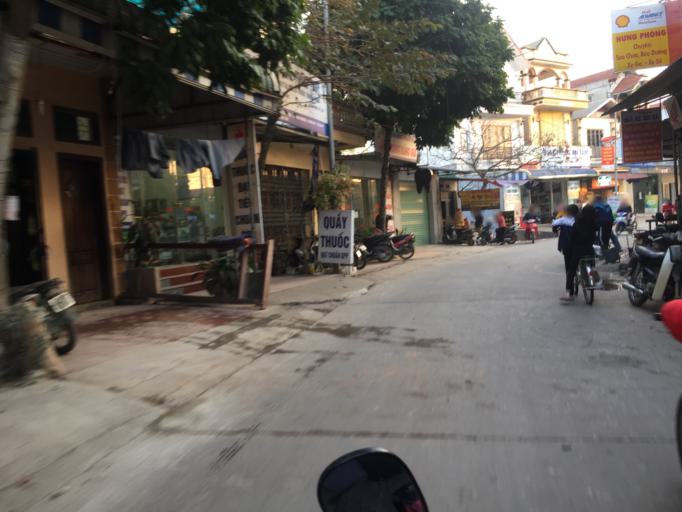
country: VN
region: Ha Noi
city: Chuc Son
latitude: 20.9012
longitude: 105.7172
